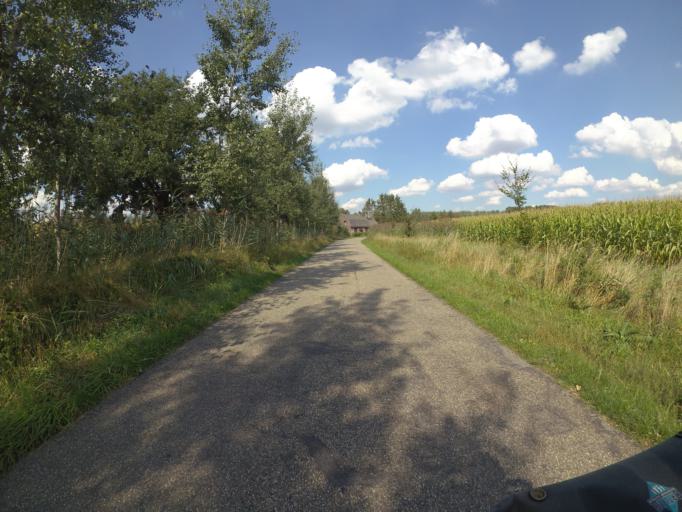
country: NL
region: North Brabant
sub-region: Gemeente Veghel
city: Eerde
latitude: 51.6173
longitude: 5.4786
